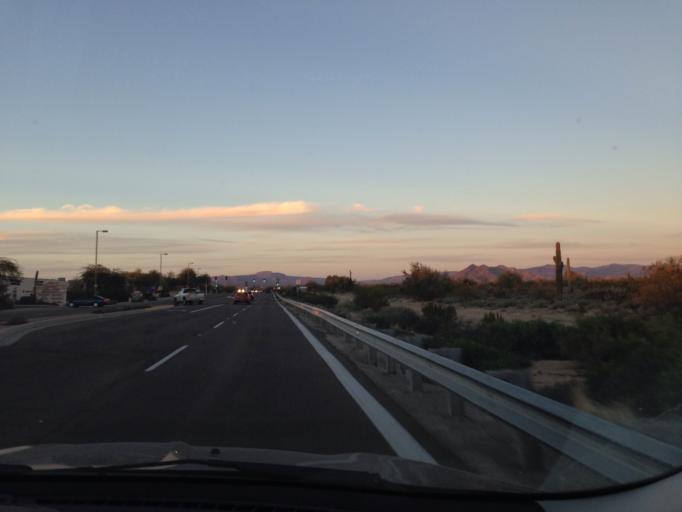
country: US
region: Arizona
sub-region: Maricopa County
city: Cave Creek
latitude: 33.7239
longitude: -111.9774
